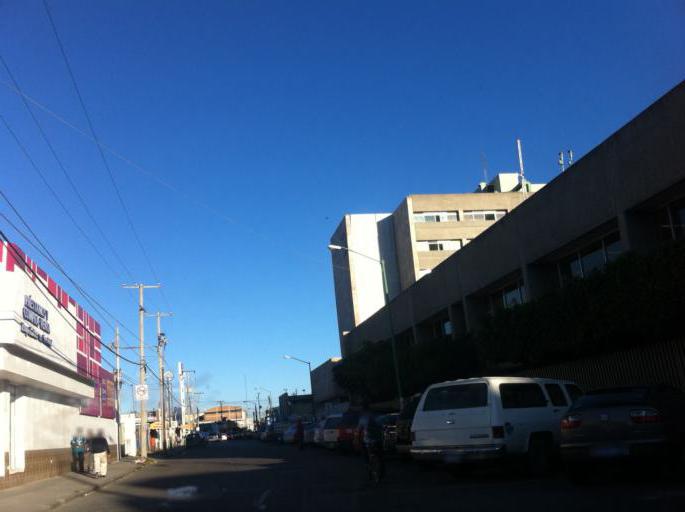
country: MX
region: Guanajuato
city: Leon
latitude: 21.1089
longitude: -101.6889
